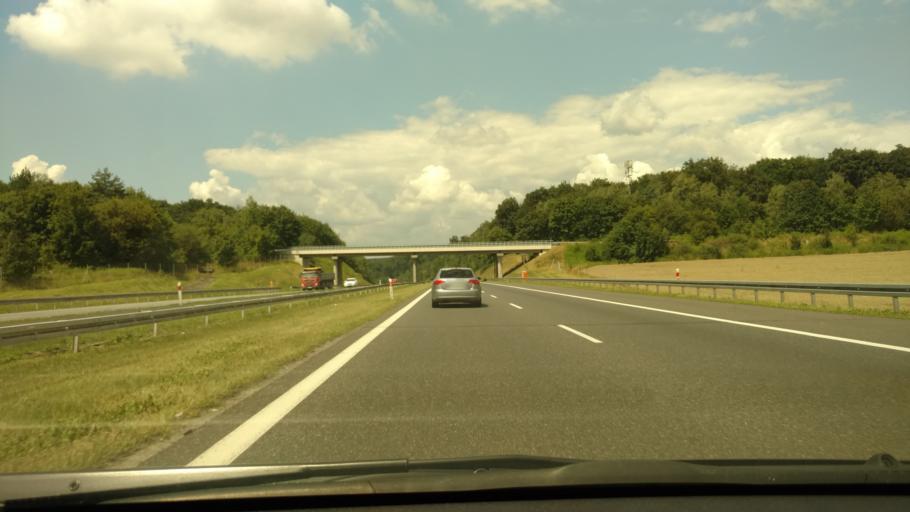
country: PL
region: Lesser Poland Voivodeship
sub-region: Powiat krakowski
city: Czulow
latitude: 50.0892
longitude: 19.6903
